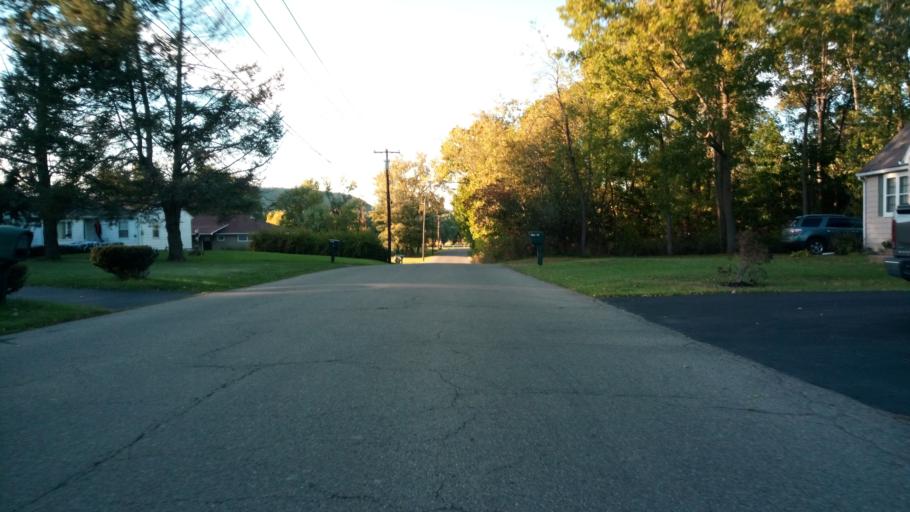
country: US
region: New York
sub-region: Chemung County
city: Elmira
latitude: 42.0758
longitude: -76.8216
